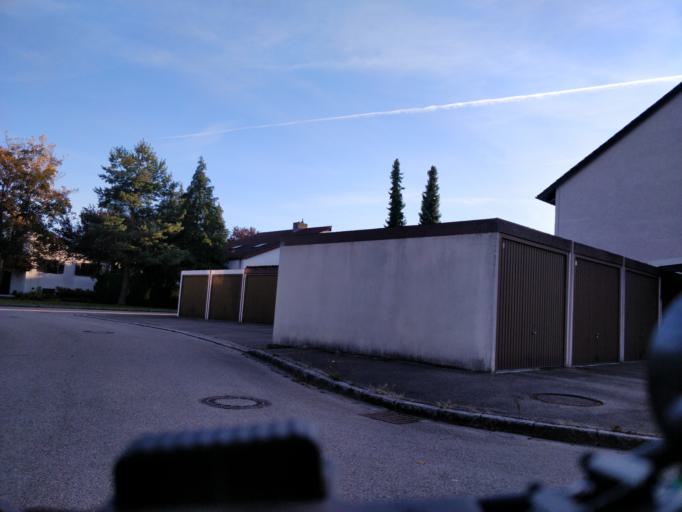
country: DE
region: Bavaria
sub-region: Swabia
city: Mering
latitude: 48.2793
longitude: 10.9698
